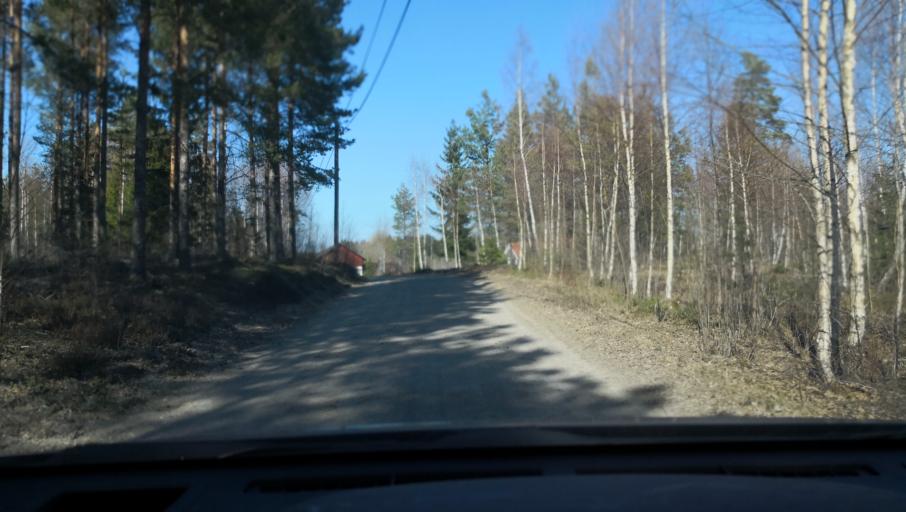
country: SE
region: Vaestmanland
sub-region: Sala Kommun
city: Sala
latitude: 59.9296
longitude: 16.4502
